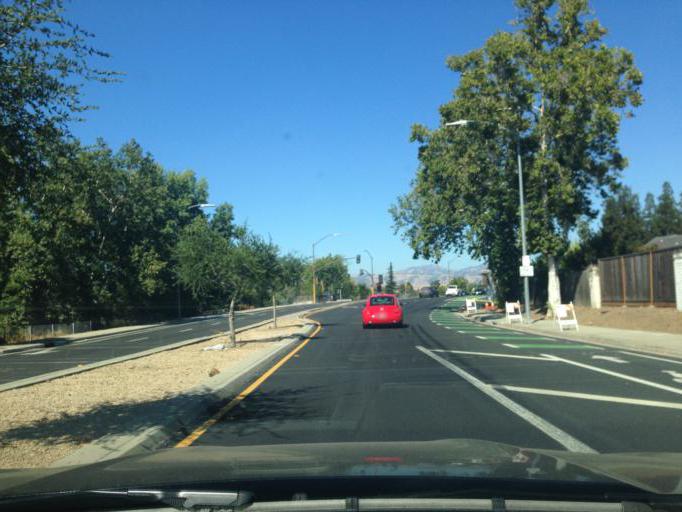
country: US
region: California
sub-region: Santa Clara County
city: Cambrian Park
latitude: 37.2374
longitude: -121.8879
